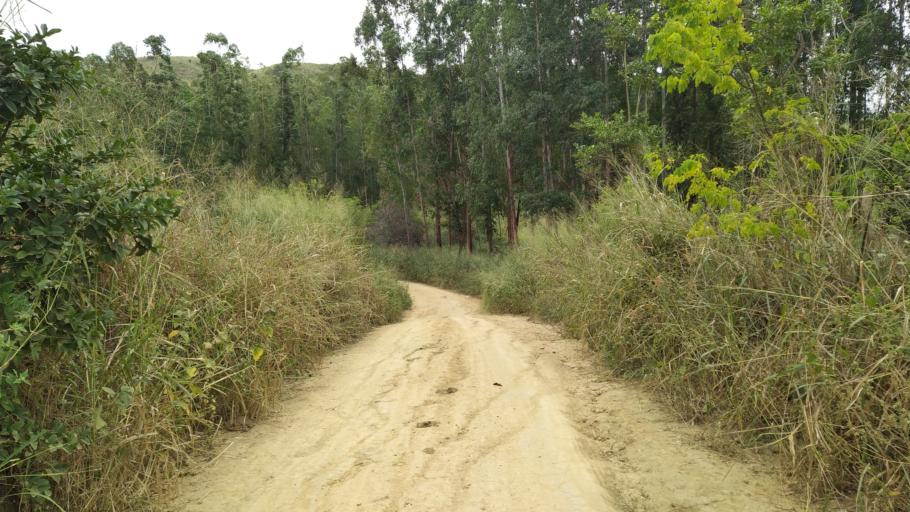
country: BR
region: Minas Gerais
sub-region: Almenara
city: Almenara
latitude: -16.6302
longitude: -40.4561
